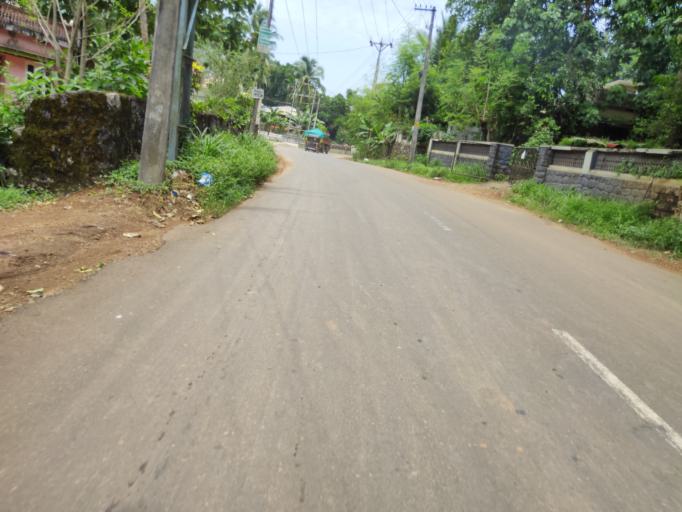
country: IN
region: Kerala
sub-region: Malappuram
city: Manjeri
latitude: 11.2018
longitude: 76.2601
